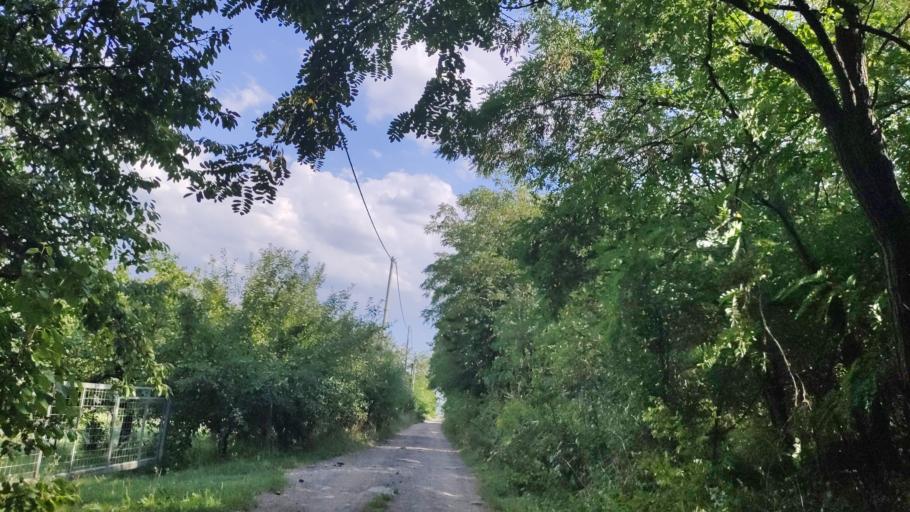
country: HU
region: Pest
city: Biatorbagy
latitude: 47.4654
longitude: 18.8628
